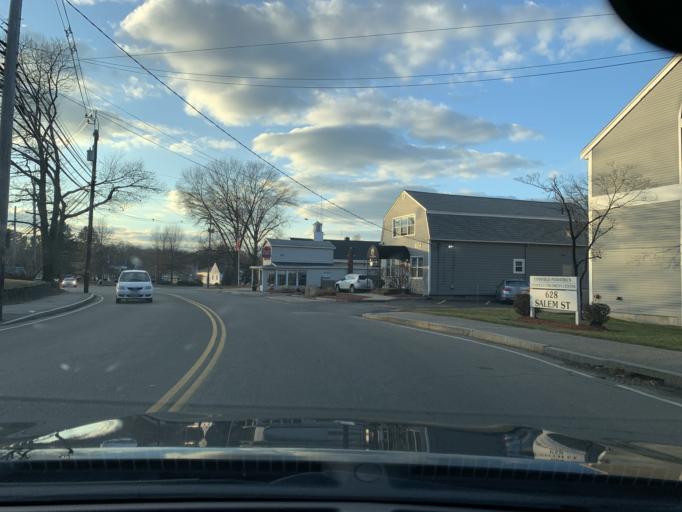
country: US
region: Massachusetts
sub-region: Essex County
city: Lynnfield
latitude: 42.5147
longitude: -71.0108
